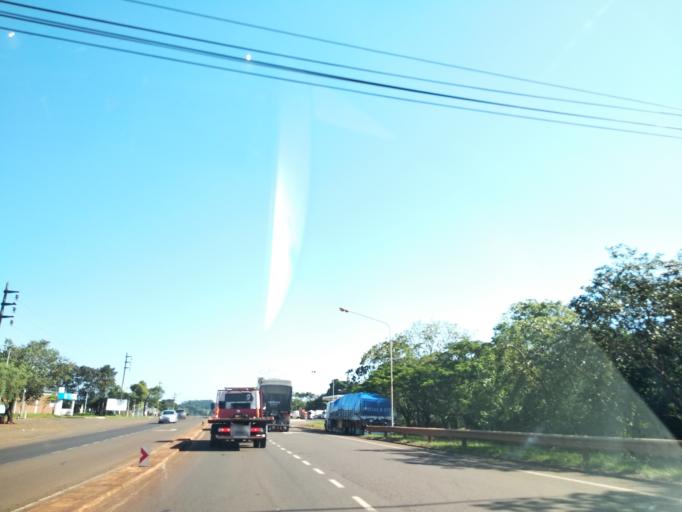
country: AR
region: Misiones
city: Puerto Rico
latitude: -26.8219
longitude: -55.0273
